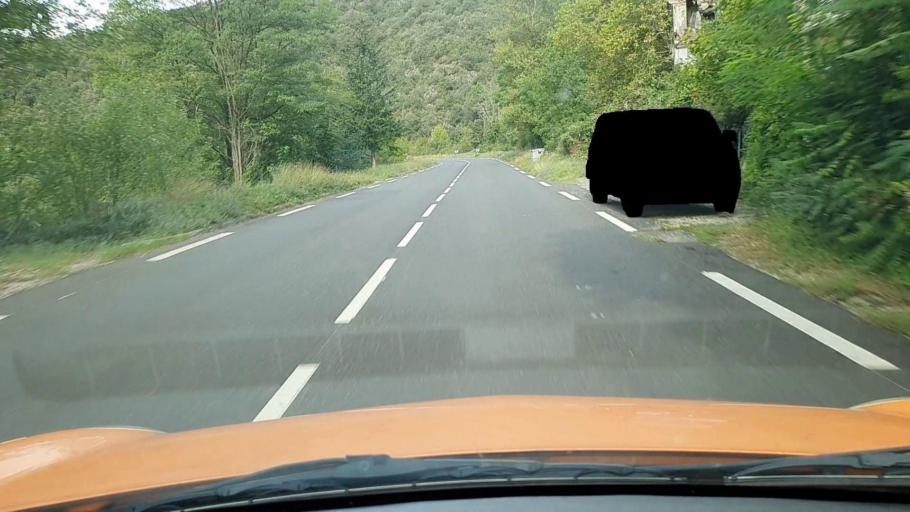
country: FR
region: Languedoc-Roussillon
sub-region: Departement du Gard
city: Valleraugue
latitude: 44.0774
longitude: 3.6664
